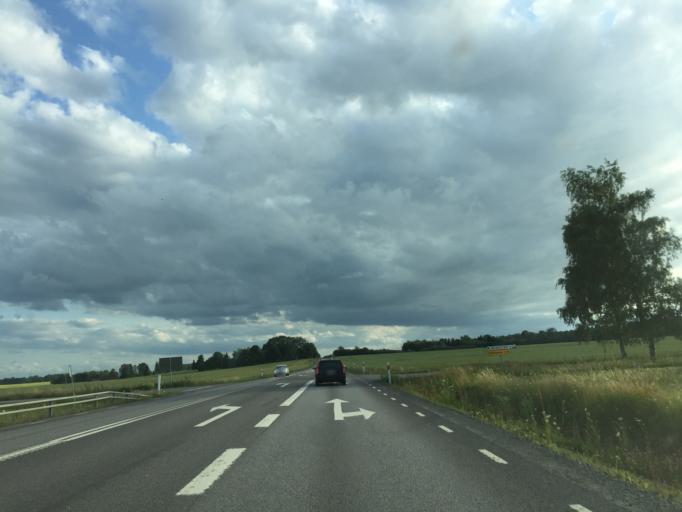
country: SE
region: OEstergoetland
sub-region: Motala Kommun
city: Motala
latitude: 58.5042
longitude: 15.0170
